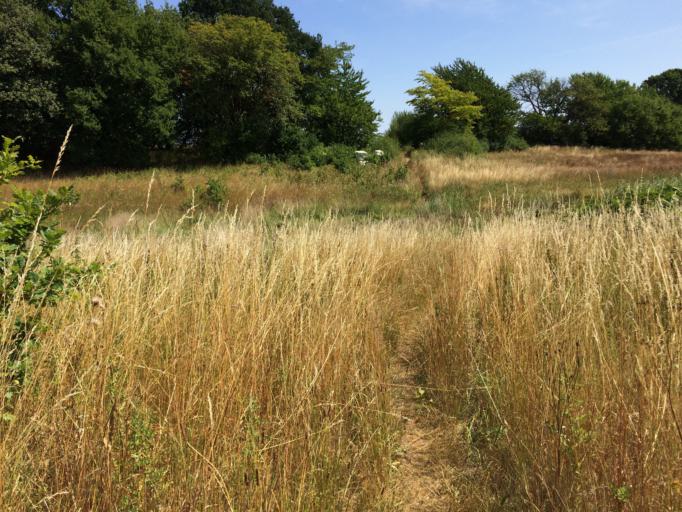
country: DK
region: Capital Region
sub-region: Fureso Kommune
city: Stavnsholt
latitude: 55.8301
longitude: 12.3996
